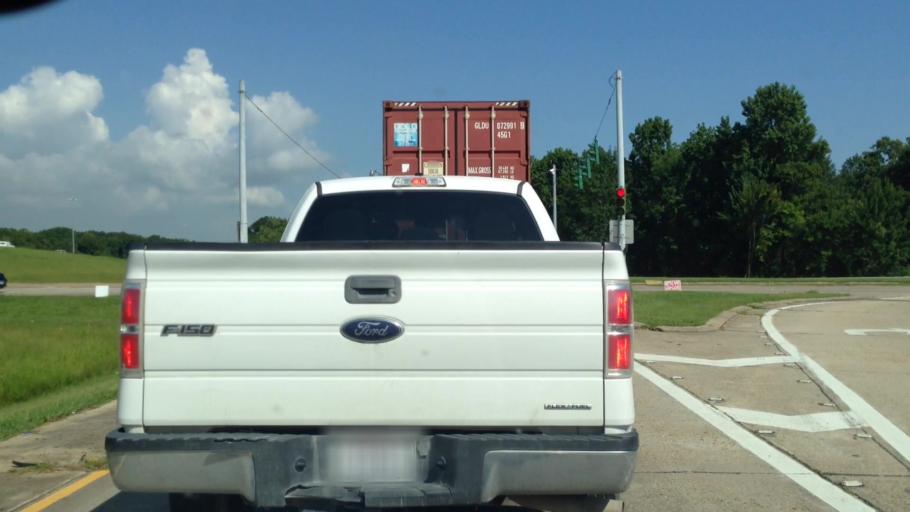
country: US
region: Louisiana
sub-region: Ascension Parish
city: Sorrento
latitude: 30.1723
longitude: -90.8756
